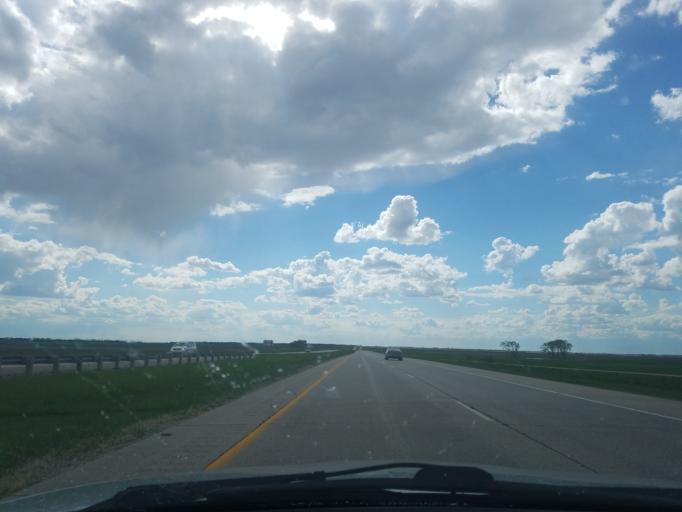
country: US
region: North Dakota
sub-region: Stutsman County
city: Jamestown
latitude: 46.8924
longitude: -98.4827
